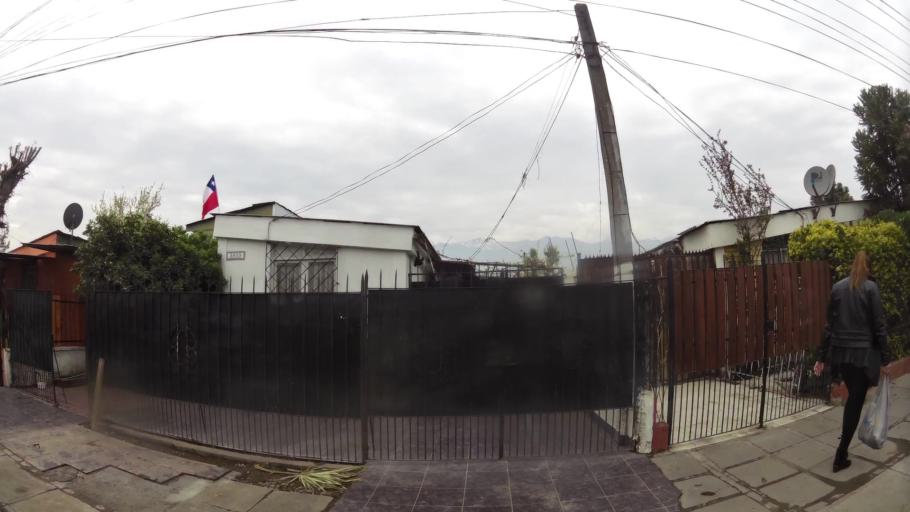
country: CL
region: Santiago Metropolitan
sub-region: Provincia de Santiago
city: Villa Presidente Frei, Nunoa, Santiago, Chile
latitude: -33.4789
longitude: -70.5917
